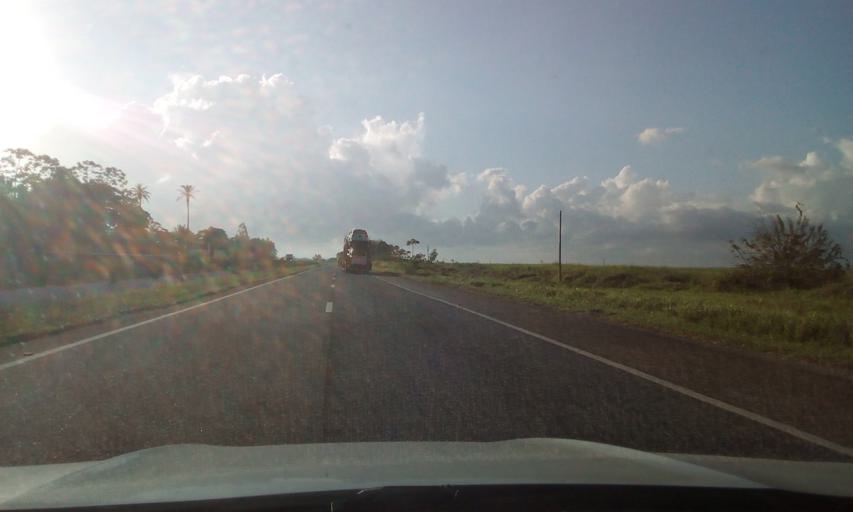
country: BR
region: Pernambuco
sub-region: Goiana
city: Goiana
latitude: -7.6446
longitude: -34.9530
